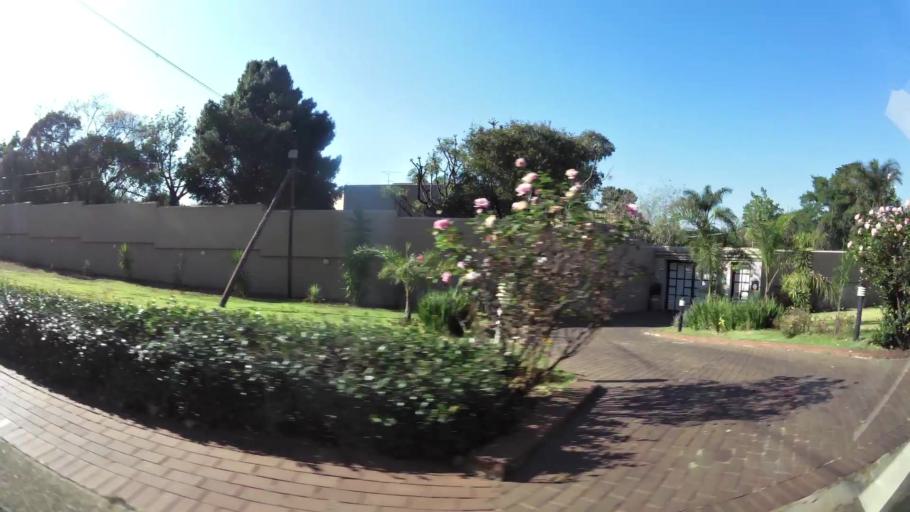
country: ZA
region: Gauteng
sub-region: City of Johannesburg Metropolitan Municipality
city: Midrand
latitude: -26.0579
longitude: 28.0311
